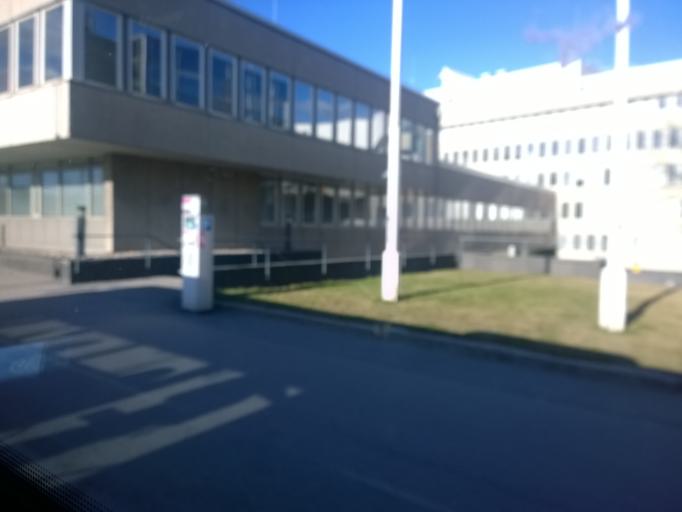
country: FI
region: Pirkanmaa
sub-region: Tampere
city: Tampere
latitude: 61.4932
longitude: 23.7709
